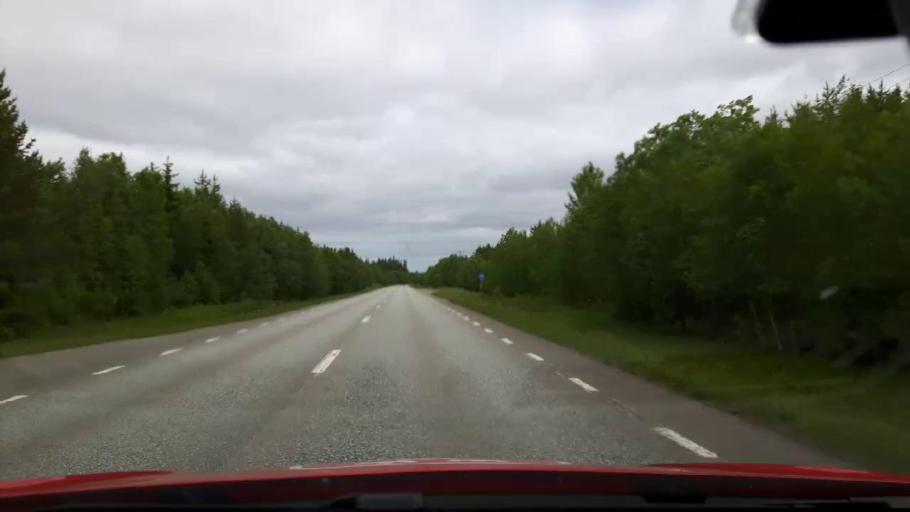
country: SE
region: Jaemtland
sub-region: Krokoms Kommun
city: Krokom
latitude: 63.5600
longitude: 14.6058
